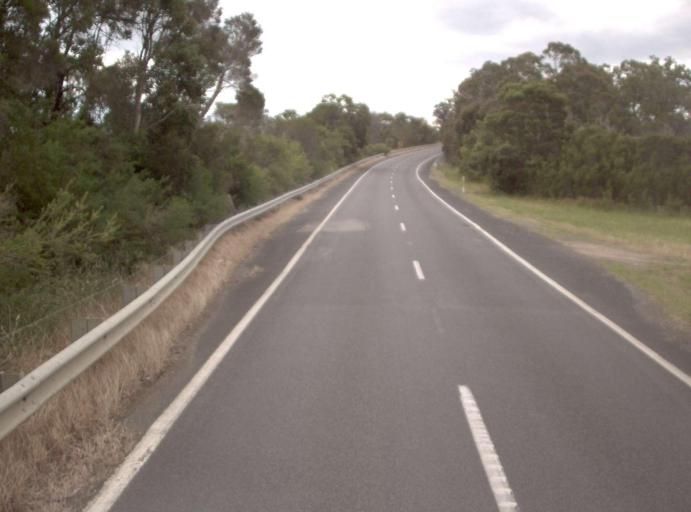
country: AU
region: Victoria
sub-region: Wellington
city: Sale
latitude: -38.2918
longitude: 147.0343
